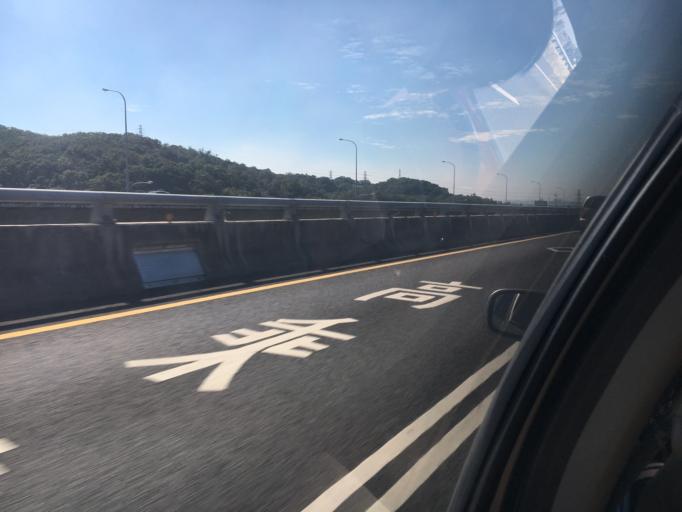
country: TW
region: Taiwan
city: Taoyuan City
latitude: 25.0474
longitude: 121.3178
